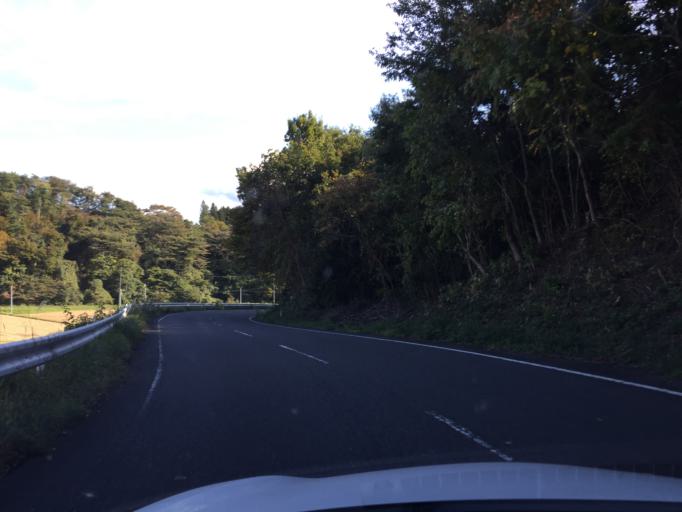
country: JP
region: Fukushima
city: Ishikawa
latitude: 37.1510
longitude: 140.5955
